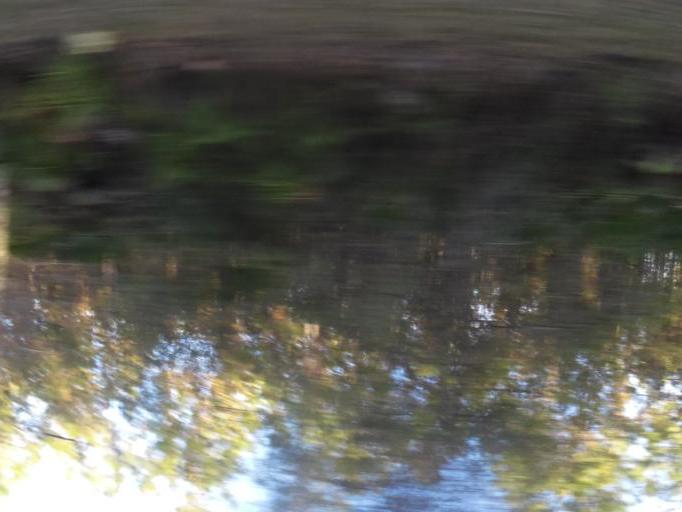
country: US
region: Florida
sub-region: Putnam County
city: East Palatka
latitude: 29.7950
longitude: -81.5114
